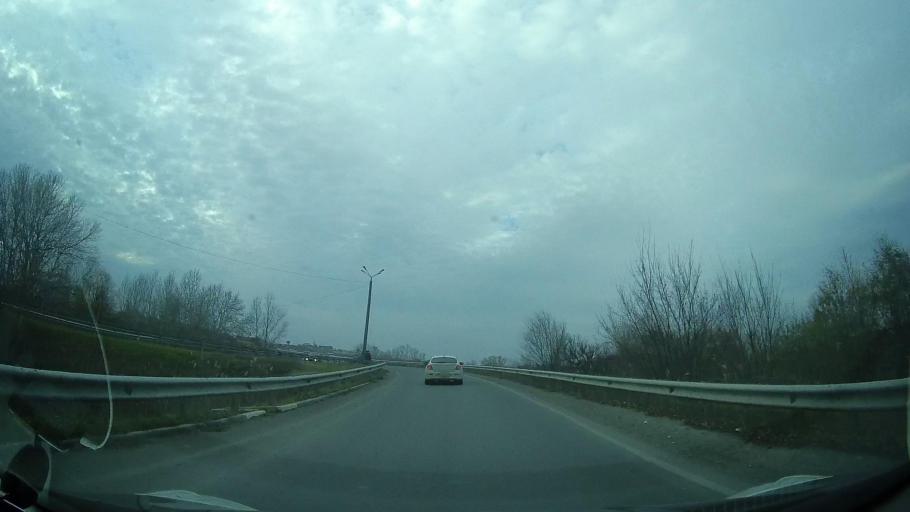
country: RU
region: Rostov
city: Aksay
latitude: 47.2392
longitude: 39.8576
